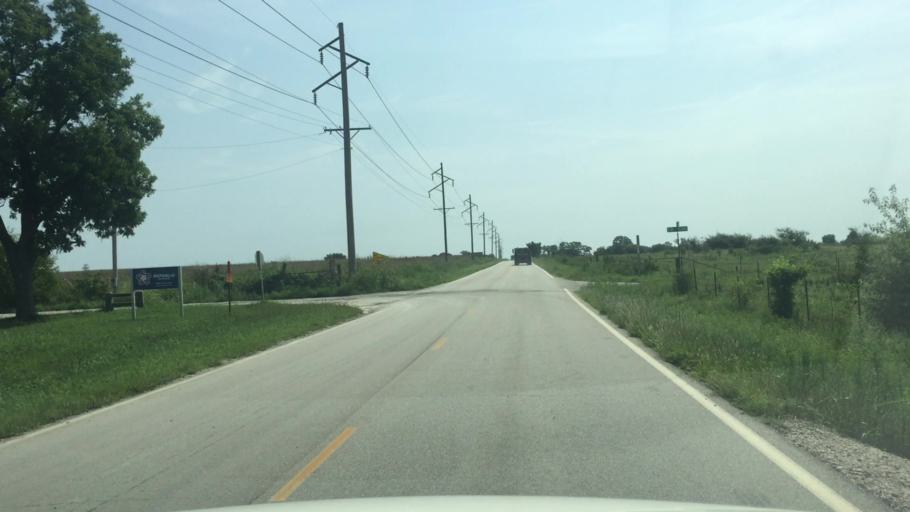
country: US
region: Kansas
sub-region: Montgomery County
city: Cherryvale
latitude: 37.2087
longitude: -95.5769
